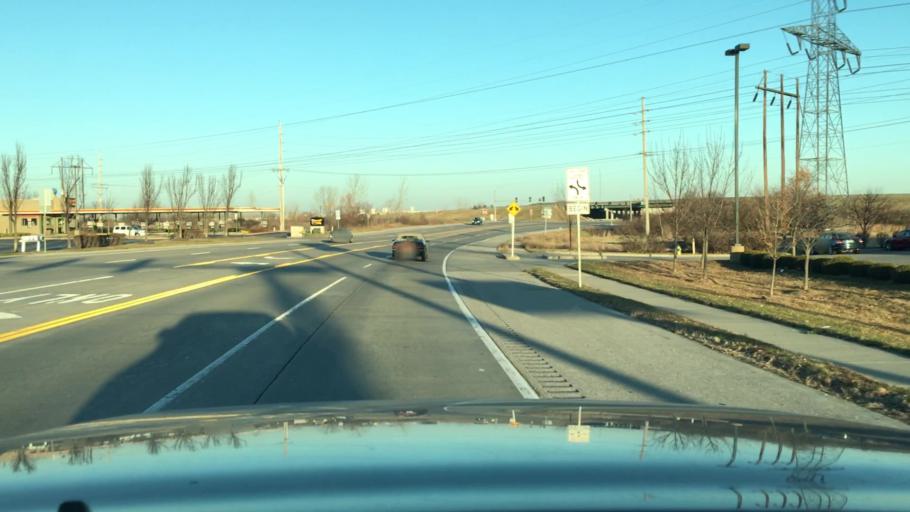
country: US
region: Missouri
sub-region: Saint Charles County
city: Saint Charles
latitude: 38.8215
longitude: -90.5163
